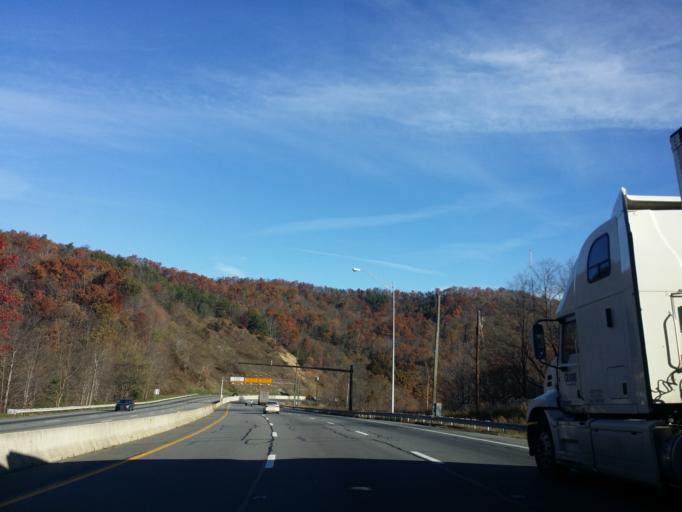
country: US
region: North Carolina
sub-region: Buncombe County
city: Black Mountain
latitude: 35.6203
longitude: -82.2395
